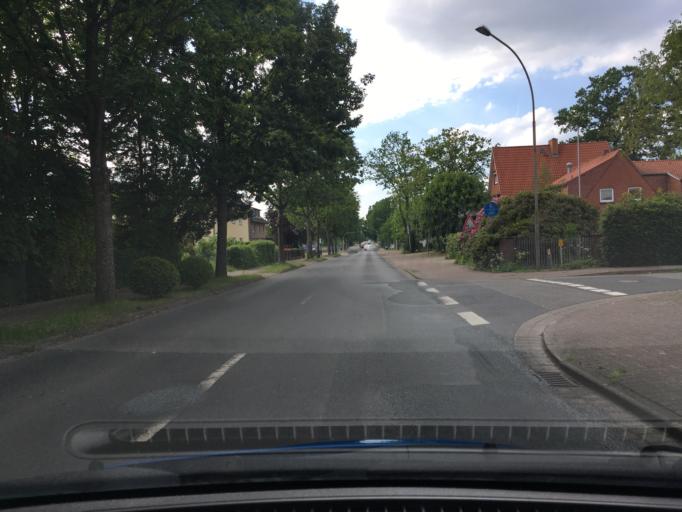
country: DE
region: Lower Saxony
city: Tostedt
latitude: 53.2666
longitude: 9.7295
